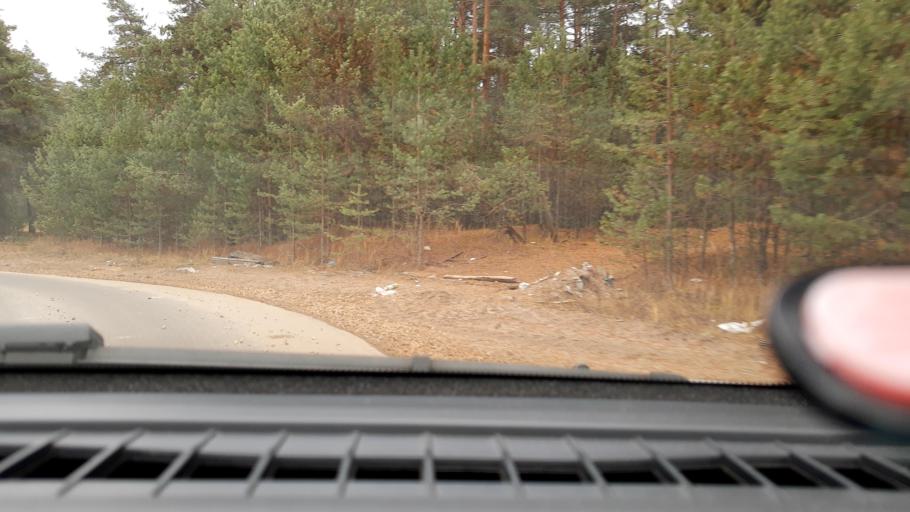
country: RU
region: Nizjnij Novgorod
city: Lukino
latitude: 56.3912
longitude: 43.7153
